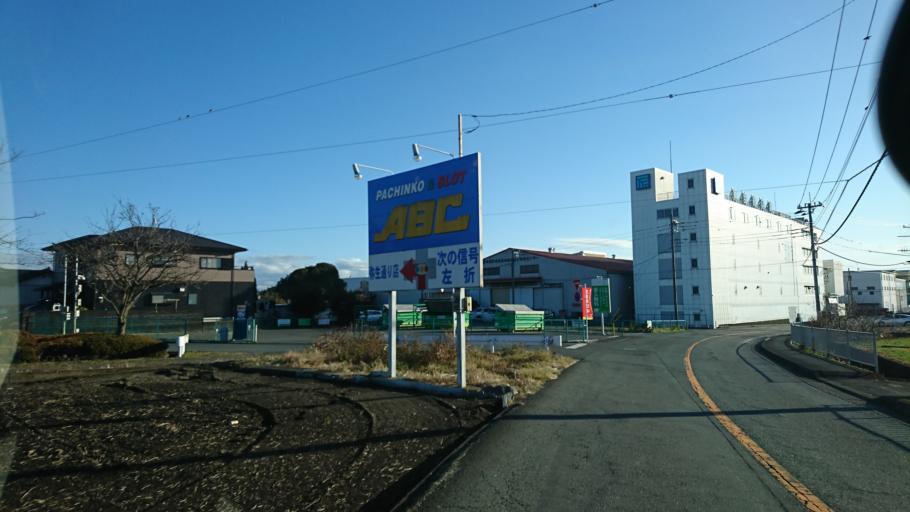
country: JP
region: Shizuoka
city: Fuji
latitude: 35.1755
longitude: 138.6571
